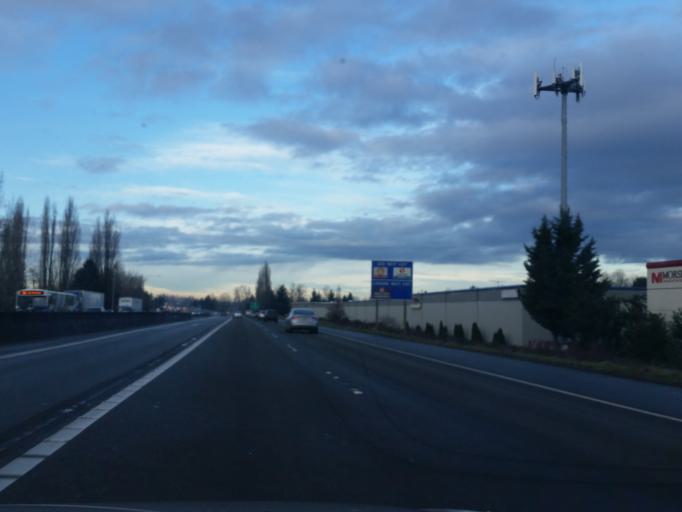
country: US
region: Washington
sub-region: King County
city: Kent
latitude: 47.3706
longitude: -122.2443
